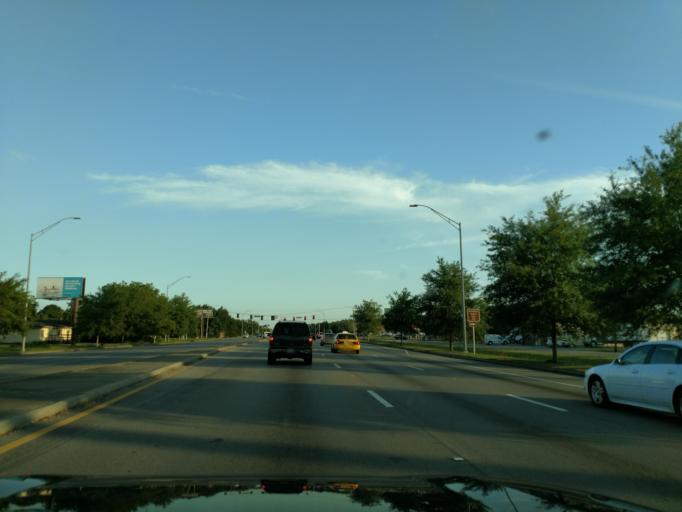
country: US
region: Mississippi
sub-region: Harrison County
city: West Gulfport
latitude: 30.4056
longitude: -89.0929
